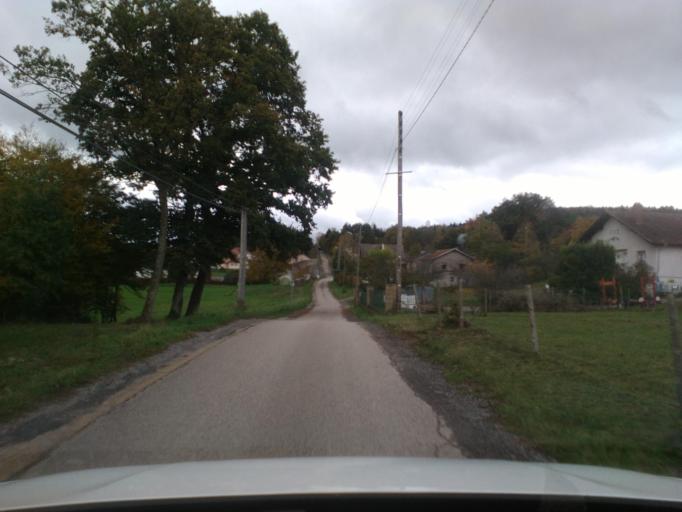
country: FR
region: Lorraine
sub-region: Departement des Vosges
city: Moyenmoutier
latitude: 48.3707
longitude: 6.8897
